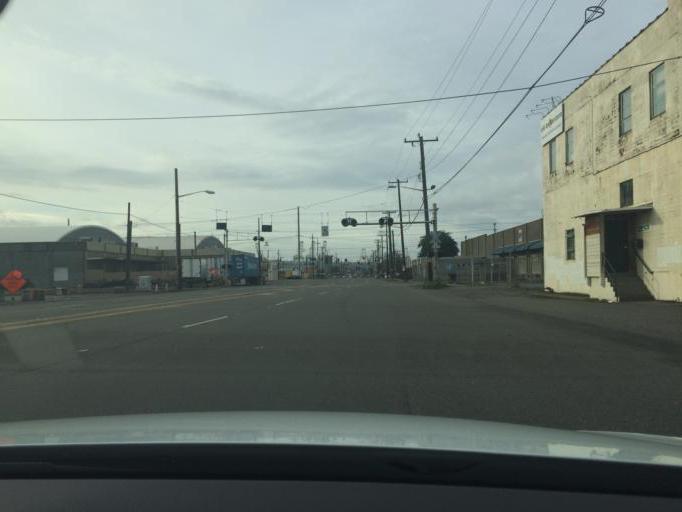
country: US
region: Washington
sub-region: King County
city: Seattle
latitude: 47.5862
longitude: -122.3237
